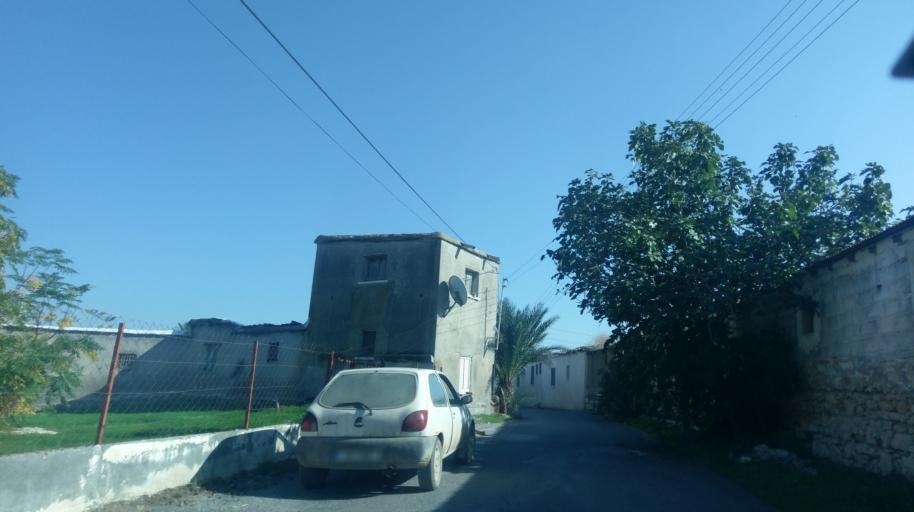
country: CY
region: Larnaka
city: Athienou
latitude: 35.1752
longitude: 33.5495
